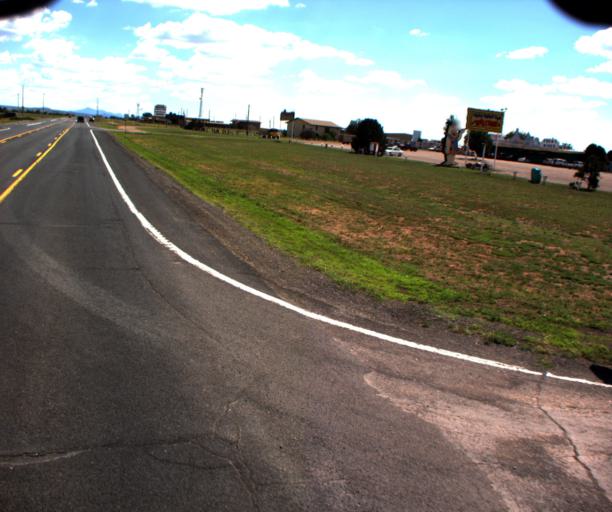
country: US
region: Arizona
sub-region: Coconino County
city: Grand Canyon Village
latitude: 35.6548
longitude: -112.1391
